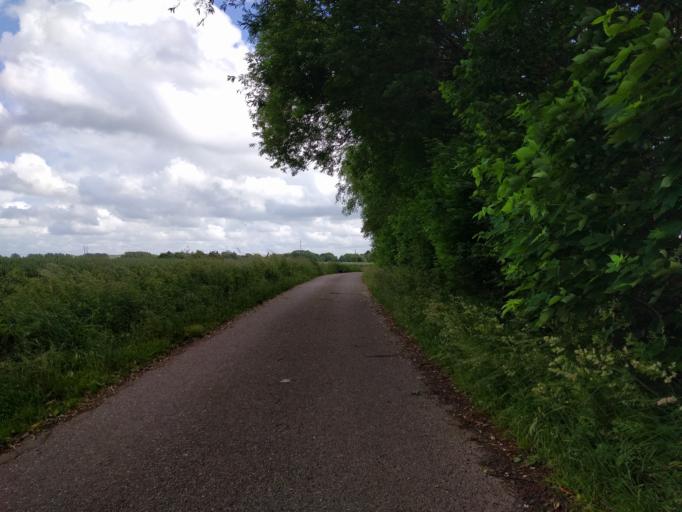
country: DK
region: South Denmark
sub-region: Kerteminde Kommune
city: Munkebo
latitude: 55.4570
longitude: 10.5132
